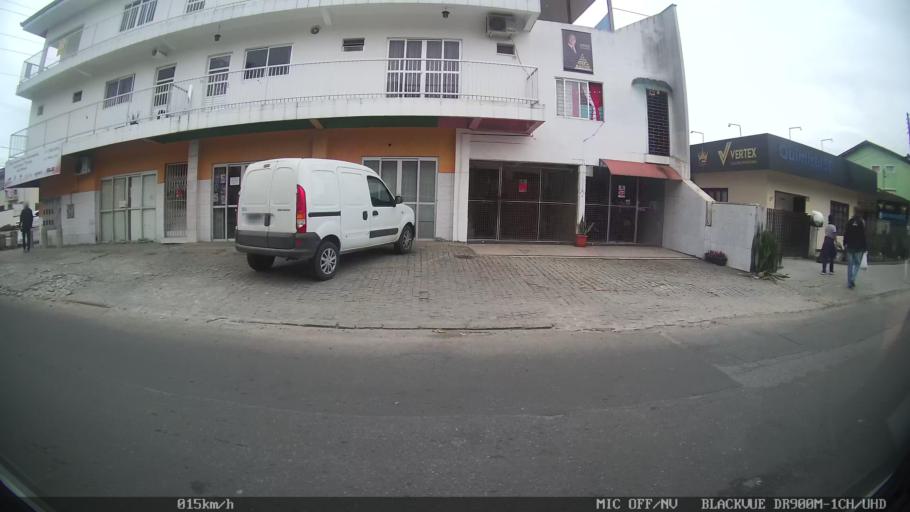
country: BR
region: Santa Catarina
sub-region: Joinville
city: Joinville
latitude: -26.2727
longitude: -48.8254
